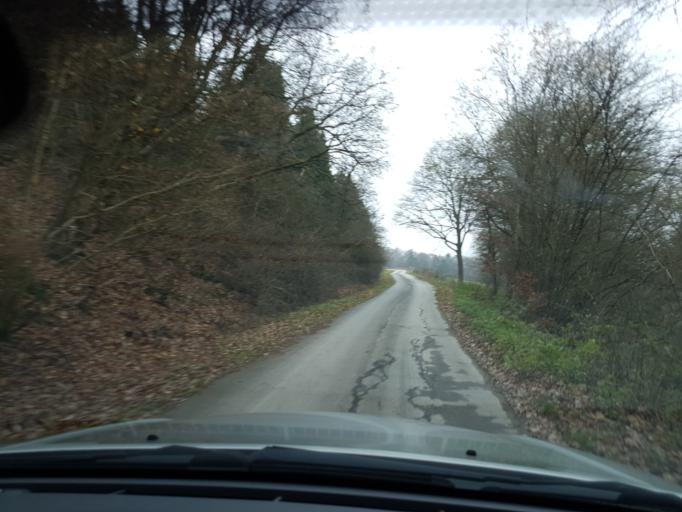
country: DE
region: Hesse
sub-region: Regierungsbezirk Darmstadt
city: Bad Schwalbach
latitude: 50.1057
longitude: 8.0253
